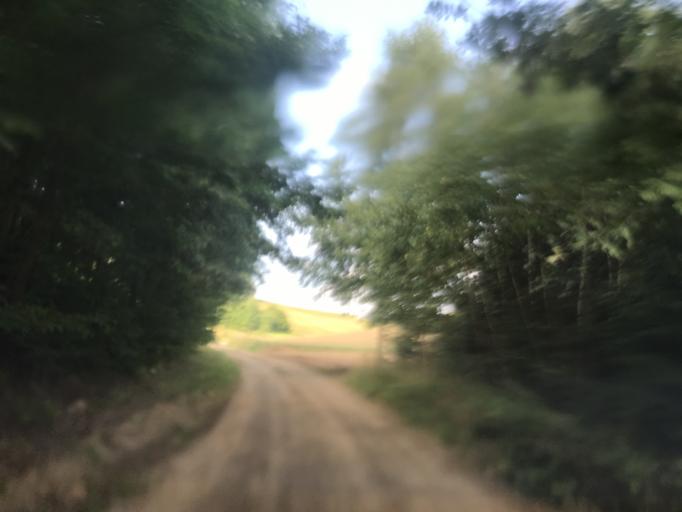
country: PL
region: Warmian-Masurian Voivodeship
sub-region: Powiat nowomiejski
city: Kurzetnik
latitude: 53.3496
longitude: 19.5086
